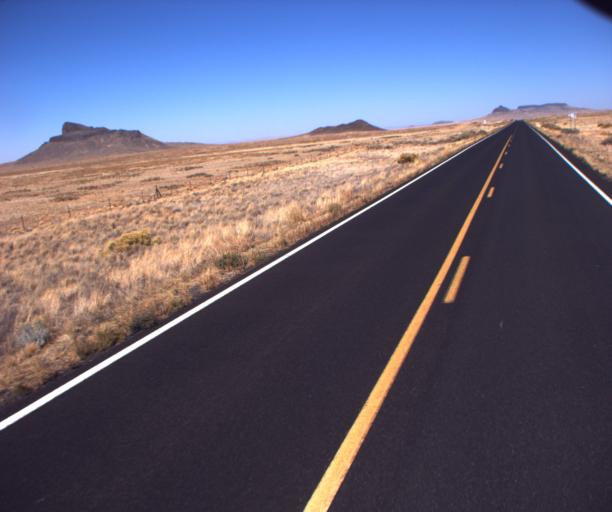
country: US
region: Arizona
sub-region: Navajo County
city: Dilkon
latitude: 35.4494
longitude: -110.4236
